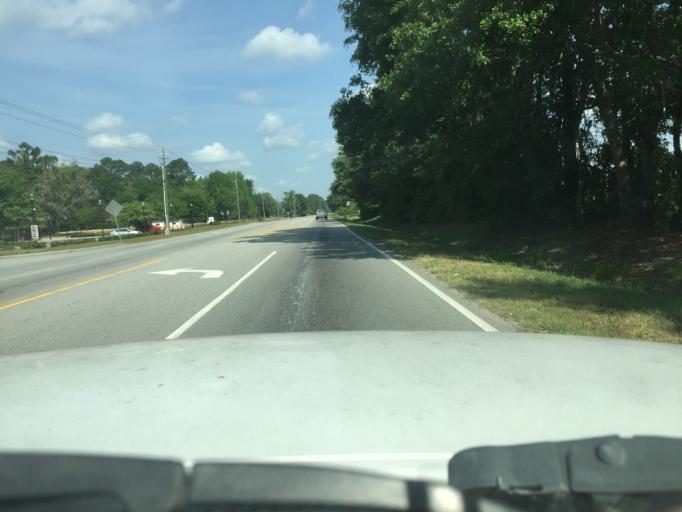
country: US
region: Georgia
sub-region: Chatham County
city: Georgetown
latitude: 32.0031
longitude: -81.2465
